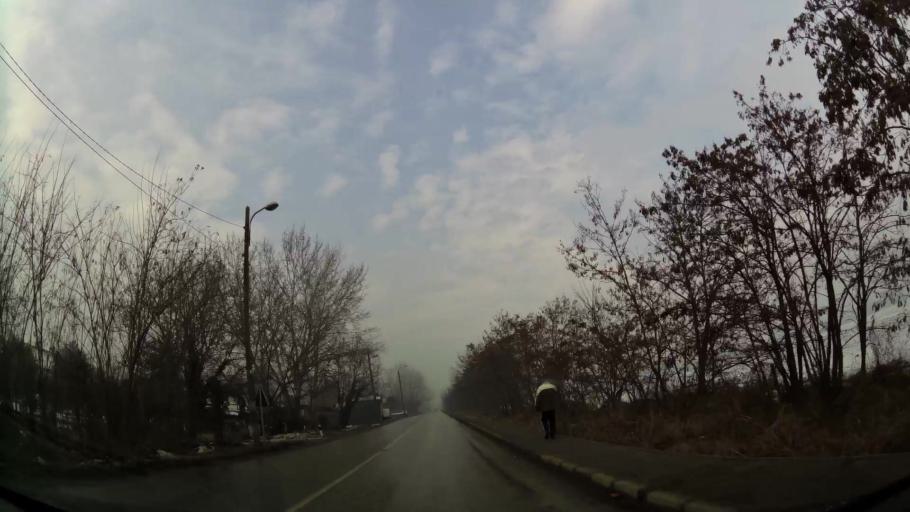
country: MK
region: Kisela Voda
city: Kisela Voda
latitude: 41.9870
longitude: 21.5170
